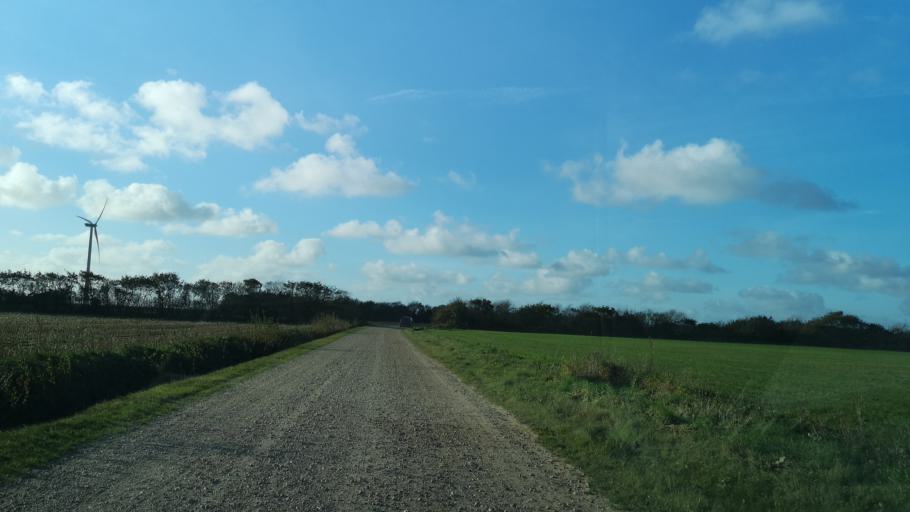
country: DK
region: Central Jutland
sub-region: Ringkobing-Skjern Kommune
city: Skjern
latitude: 55.8640
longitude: 8.3374
